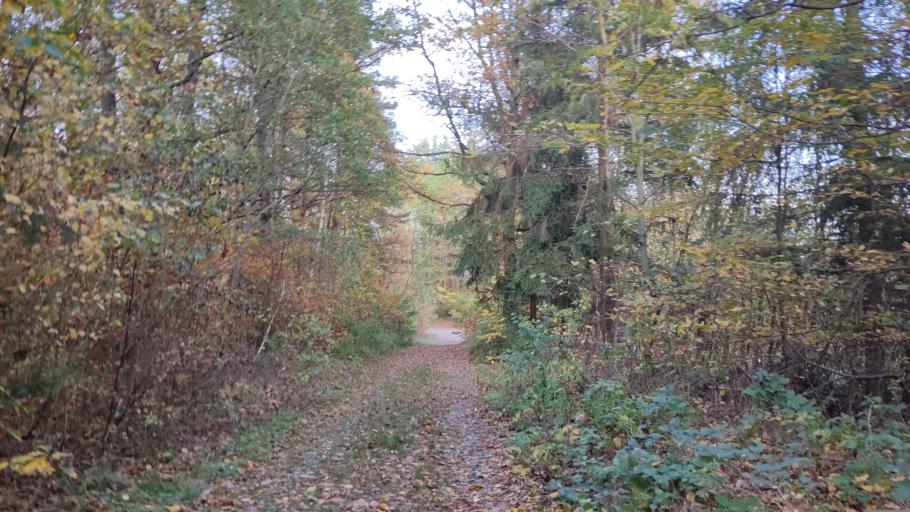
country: DE
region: Saxony
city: Struppen
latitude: 50.9009
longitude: 14.0362
